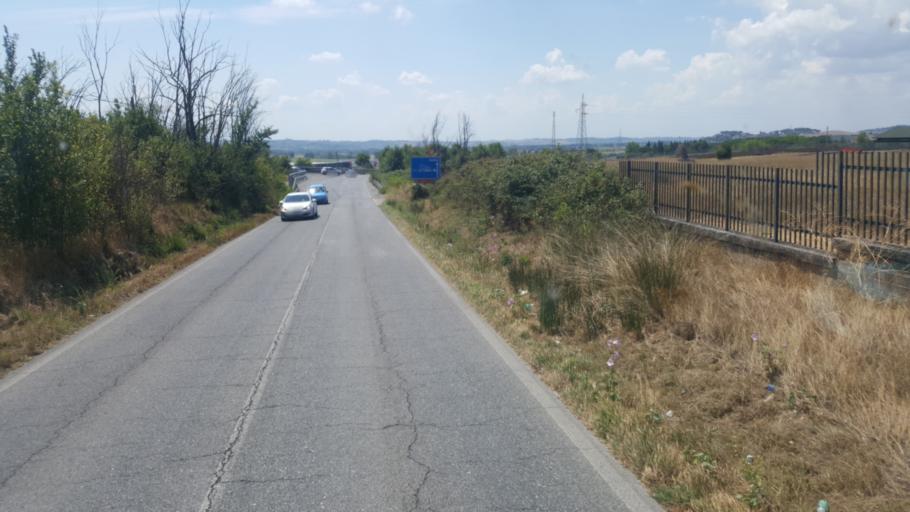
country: IT
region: Latium
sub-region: Citta metropolitana di Roma Capitale
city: Bivio di Capanelle
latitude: 42.1309
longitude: 12.5983
